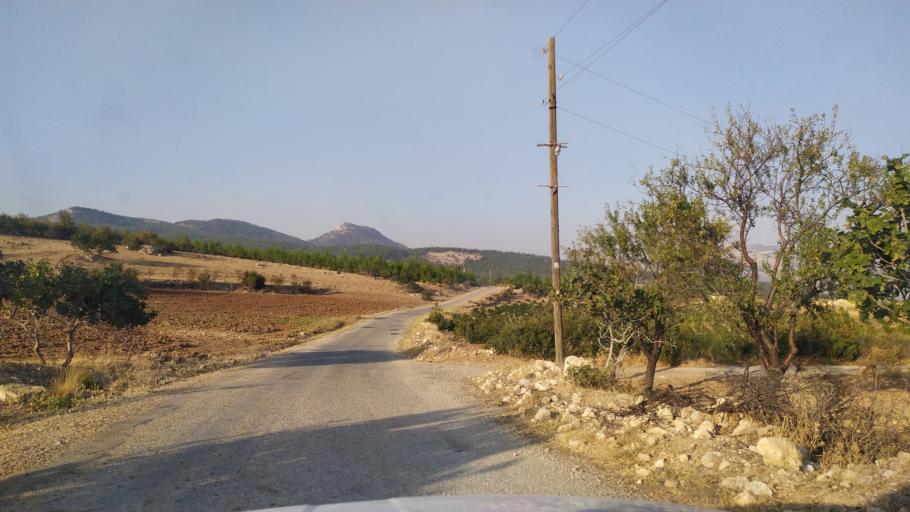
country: TR
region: Mersin
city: Mut
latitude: 36.6834
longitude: 33.1926
